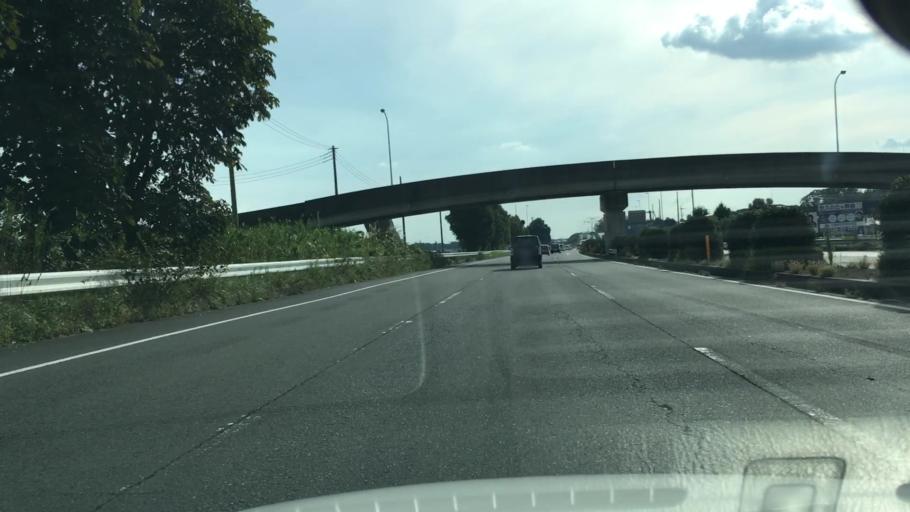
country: JP
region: Tochigi
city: Utsunomiya-shi
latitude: 36.5416
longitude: 139.9354
